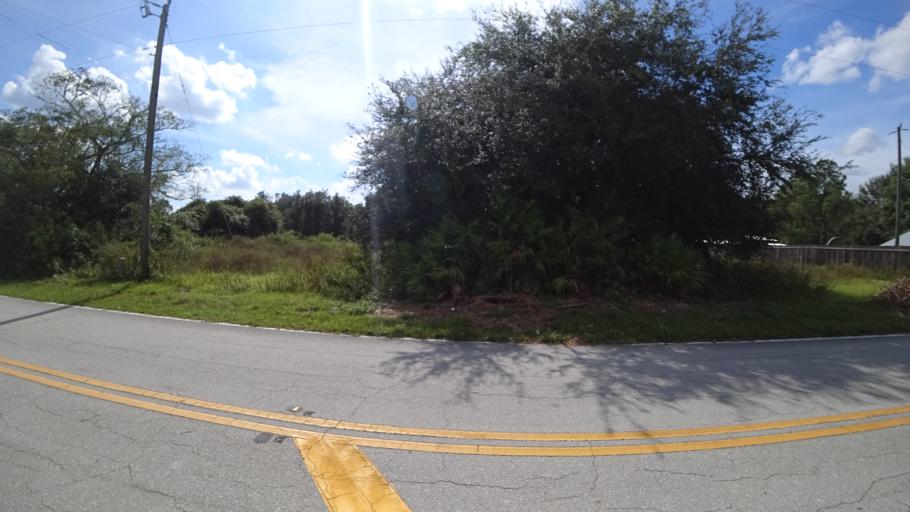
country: US
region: Florida
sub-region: Hardee County
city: Wauchula
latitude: 27.4690
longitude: -82.0764
